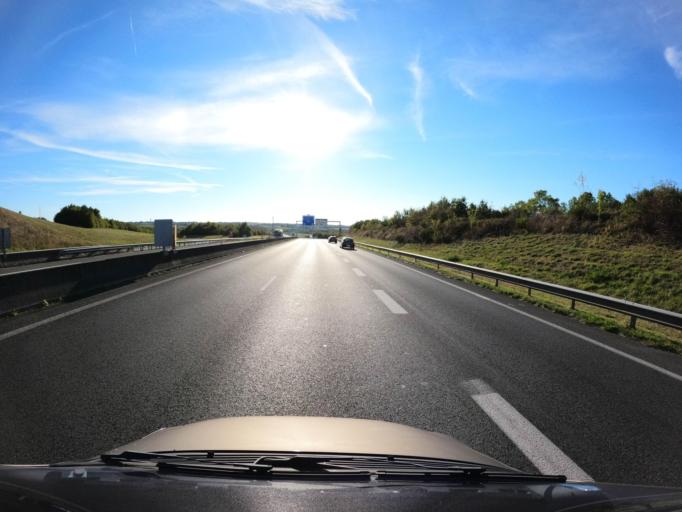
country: FR
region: Pays de la Loire
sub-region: Departement de Maine-et-Loire
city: Murs-Erigne
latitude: 47.3939
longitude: -0.5387
